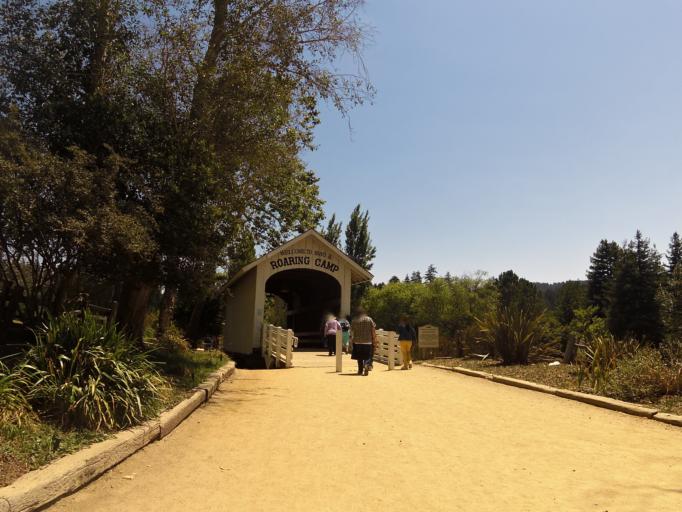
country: US
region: California
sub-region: Santa Cruz County
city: Mount Hermon
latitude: 37.0431
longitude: -122.0632
